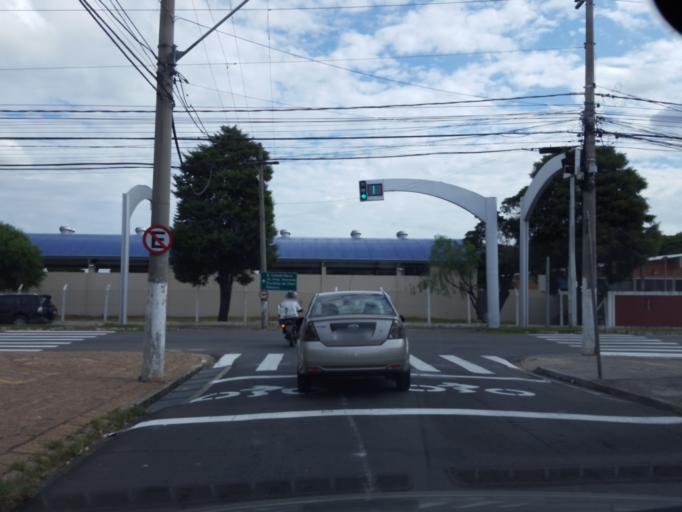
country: BR
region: Sao Paulo
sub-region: Indaiatuba
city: Indaiatuba
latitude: -23.0787
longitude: -47.1990
